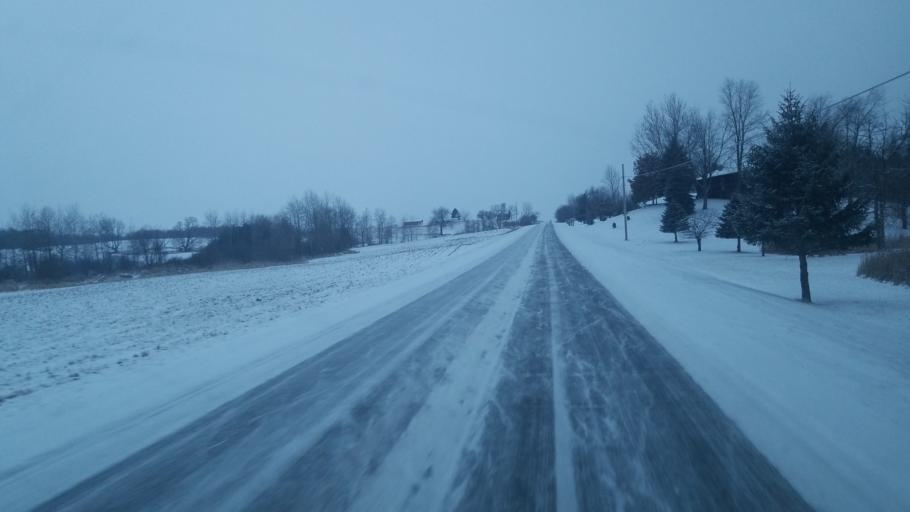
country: US
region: Michigan
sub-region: Osceola County
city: Reed City
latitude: 43.8437
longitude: -85.4479
